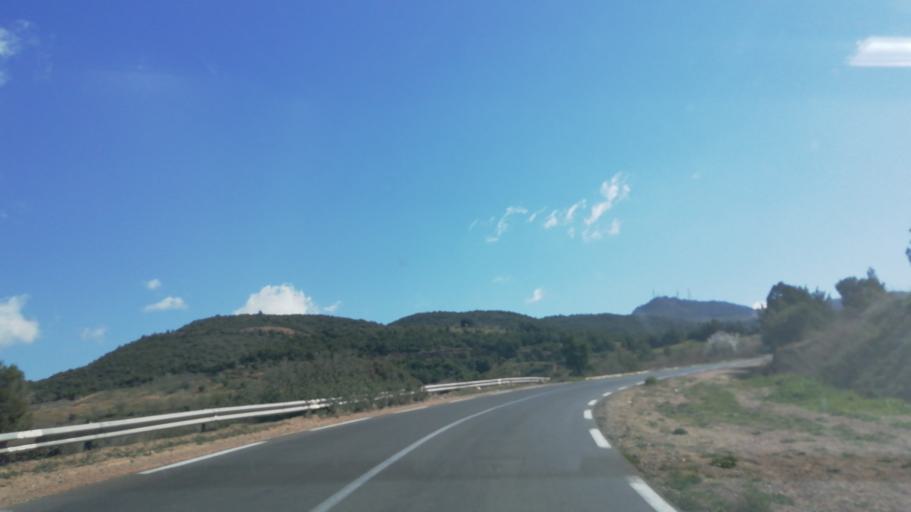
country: DZ
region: Mascara
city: Mascara
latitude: 35.4898
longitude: 0.1399
